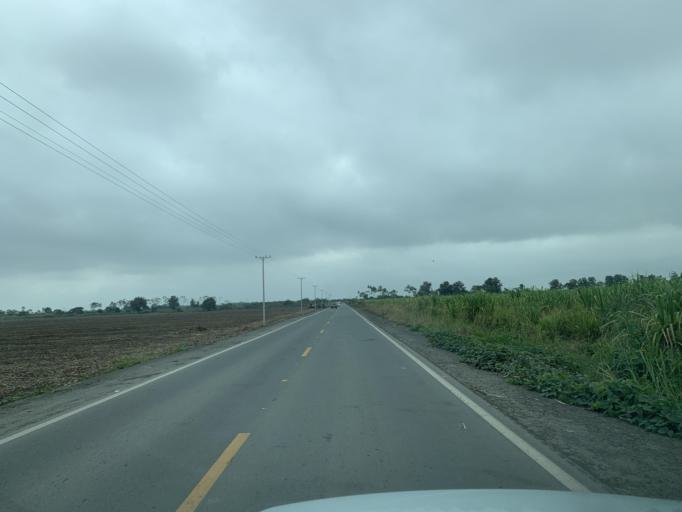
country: EC
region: Guayas
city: Coronel Marcelino Mariduena
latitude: -2.3071
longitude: -79.5067
